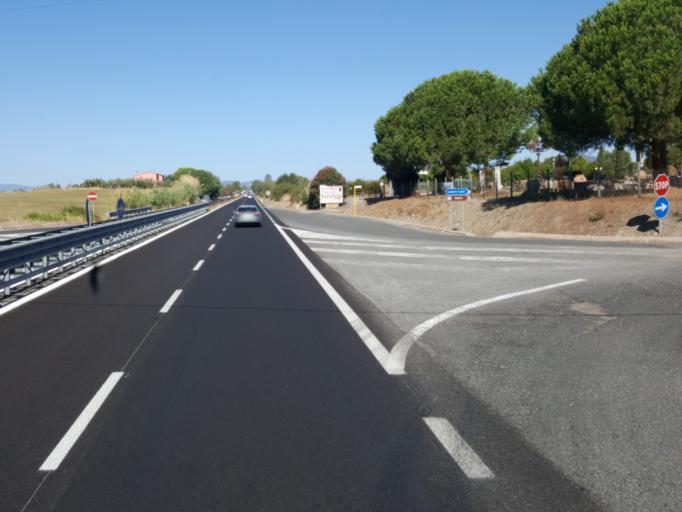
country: IT
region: Latium
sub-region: Provincia di Viterbo
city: Pescia Romana
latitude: 42.3956
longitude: 11.5237
